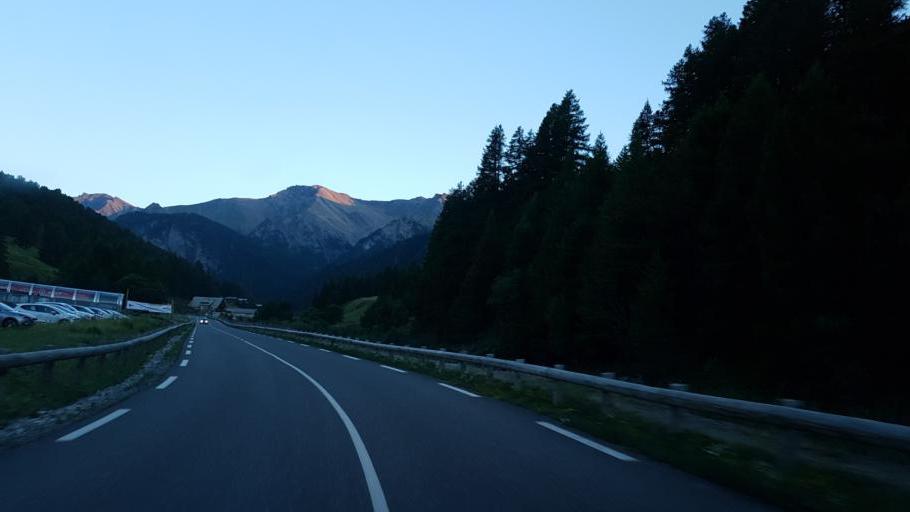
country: FR
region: Provence-Alpes-Cote d'Azur
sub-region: Departement des Hautes-Alpes
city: Guillestre
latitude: 44.7214
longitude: 6.8459
